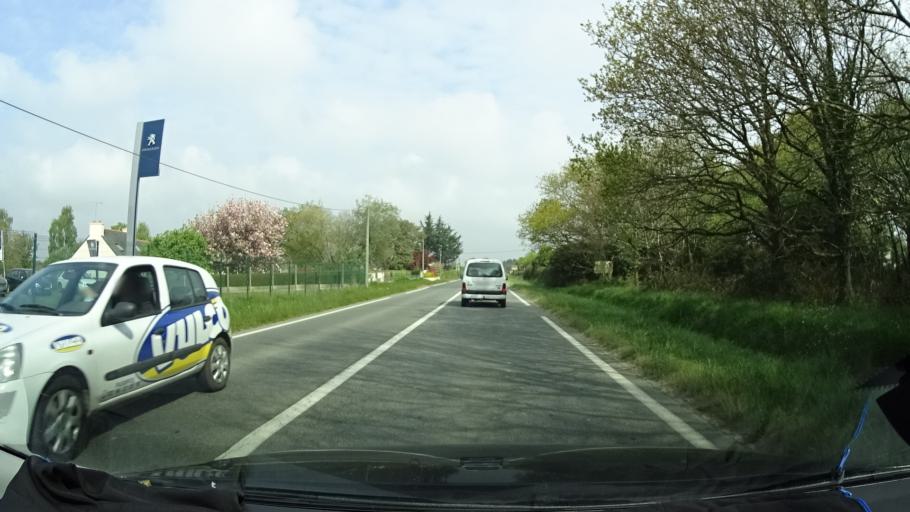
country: FR
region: Brittany
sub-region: Departement des Cotes-d'Armor
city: Paimpol
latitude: 48.7485
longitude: -3.0389
